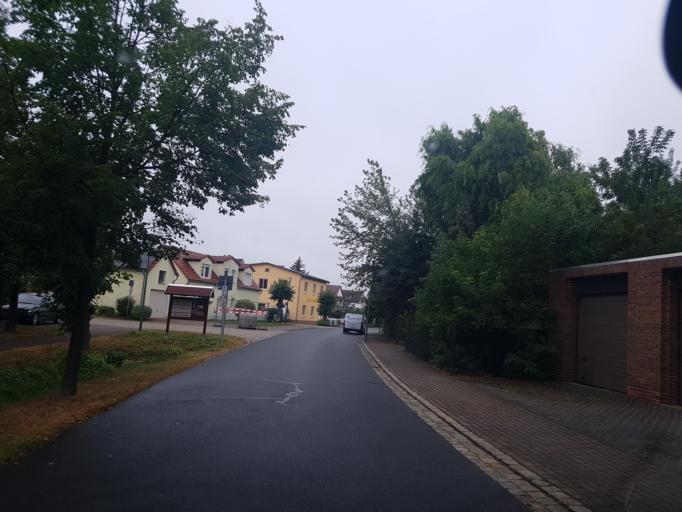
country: DE
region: Brandenburg
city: Elsterwerda
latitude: 51.4577
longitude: 13.5258
